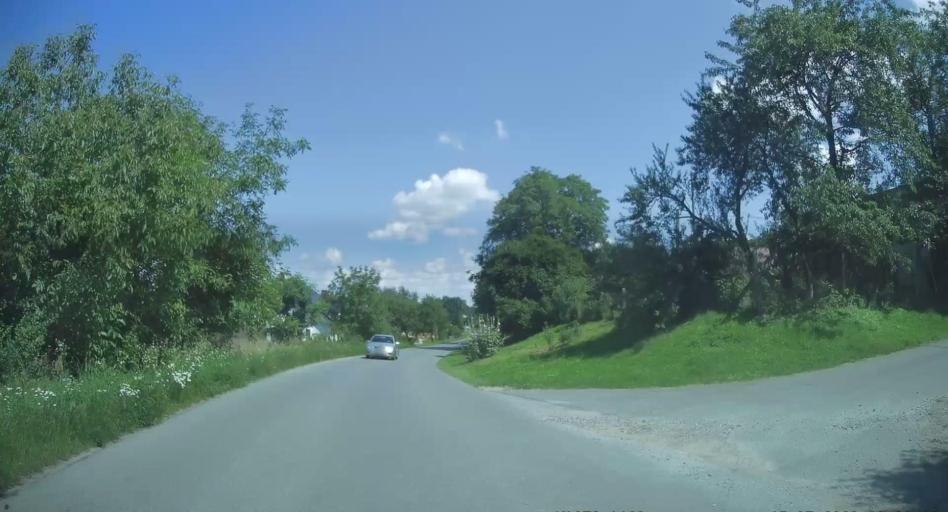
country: PL
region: Subcarpathian Voivodeship
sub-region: Powiat jaroslawski
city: Sosnica
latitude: 49.8607
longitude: 22.8810
